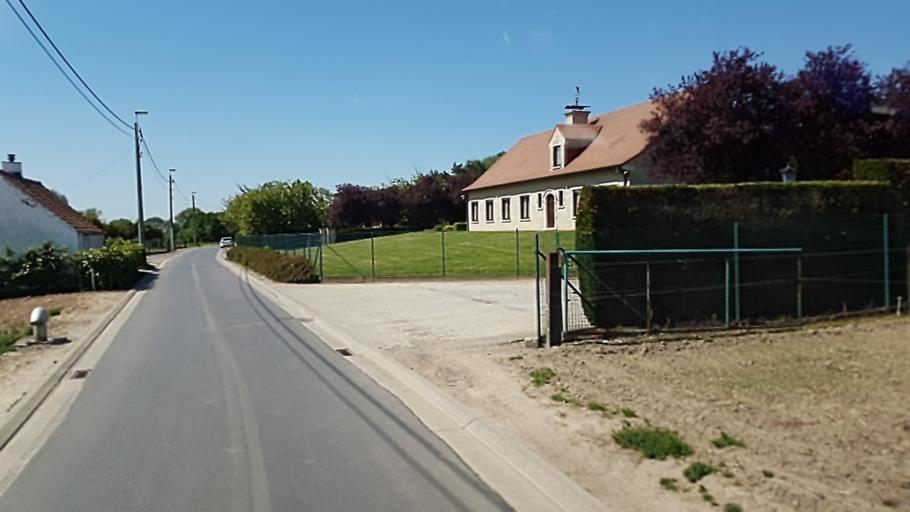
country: BE
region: Flanders
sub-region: Provincie Vlaams-Brabant
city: Ternat
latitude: 50.9005
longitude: 4.1571
